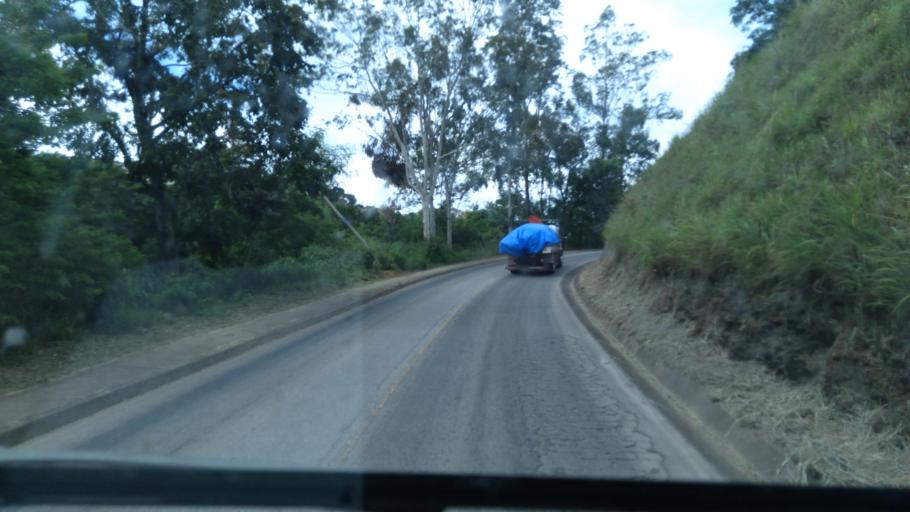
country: BR
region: Minas Gerais
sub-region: Belo Horizonte
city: Belo Horizonte
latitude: -19.8746
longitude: -43.8583
